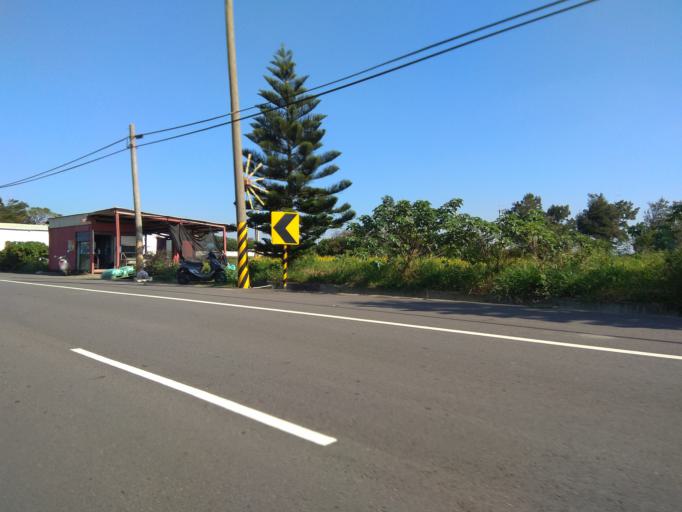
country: TW
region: Taiwan
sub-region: Hsinchu
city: Zhubei
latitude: 25.0208
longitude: 121.0572
